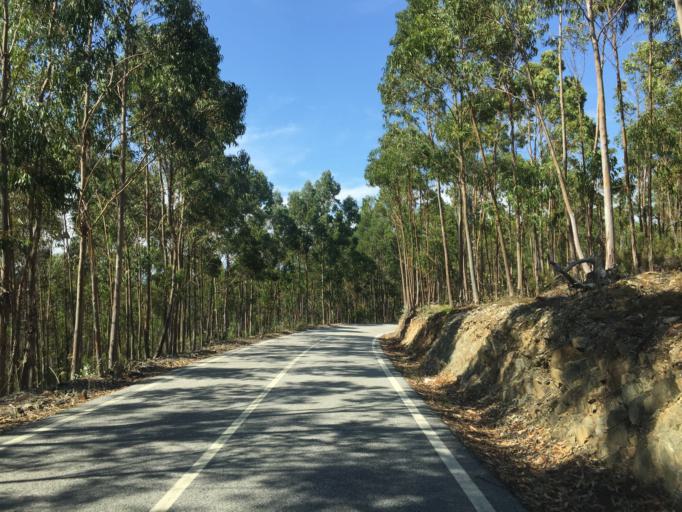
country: PT
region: Castelo Branco
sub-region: Oleiros
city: Oleiros
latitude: 39.9901
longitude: -7.8449
